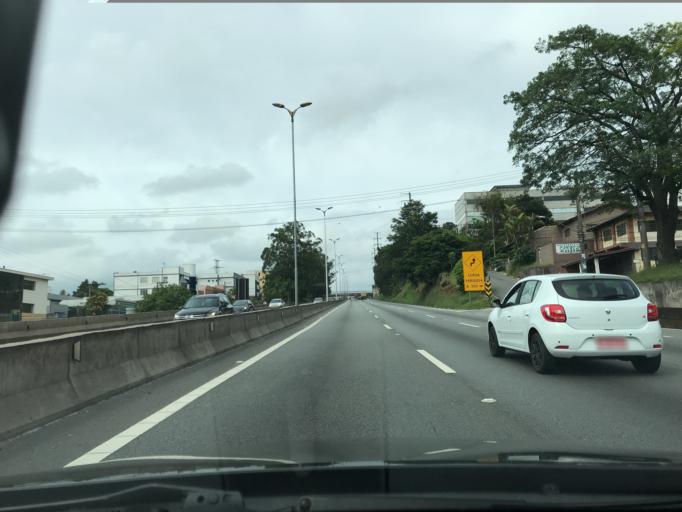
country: BR
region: Sao Paulo
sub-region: Embu
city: Embu
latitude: -23.5977
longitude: -46.8422
